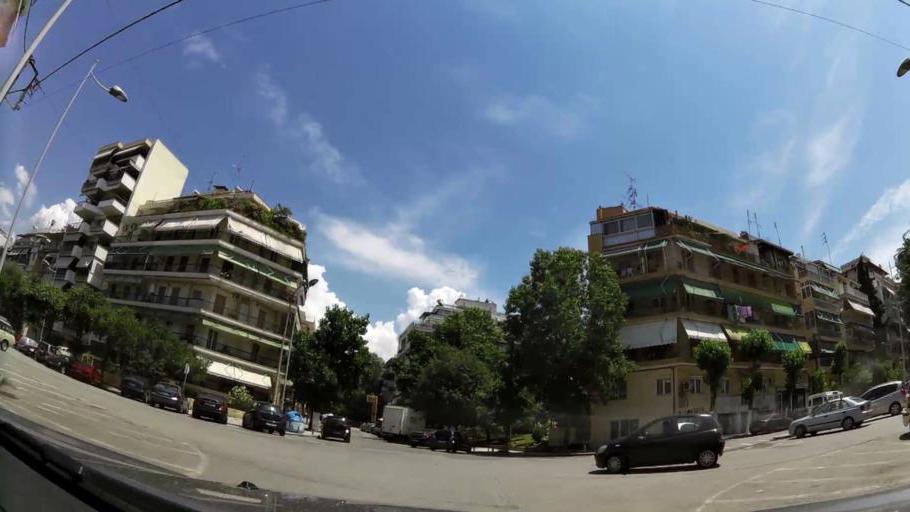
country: GR
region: Central Macedonia
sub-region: Nomos Thessalonikis
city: Triandria
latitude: 40.6090
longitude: 22.9604
